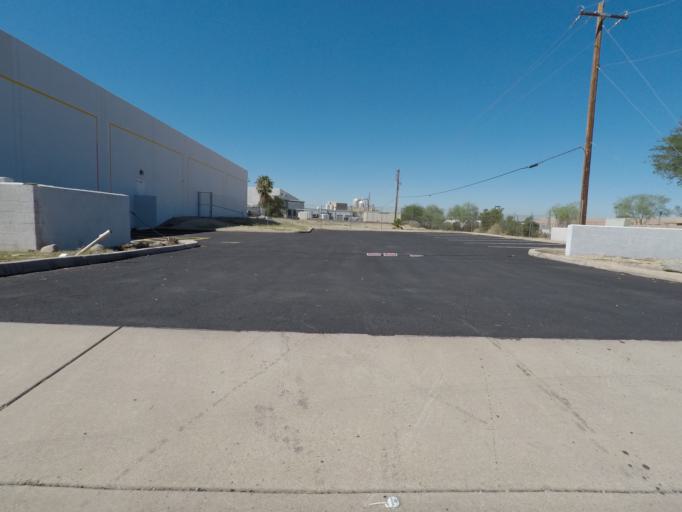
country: US
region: Arizona
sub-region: Maricopa County
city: Tempe Junction
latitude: 33.4054
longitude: -111.9479
